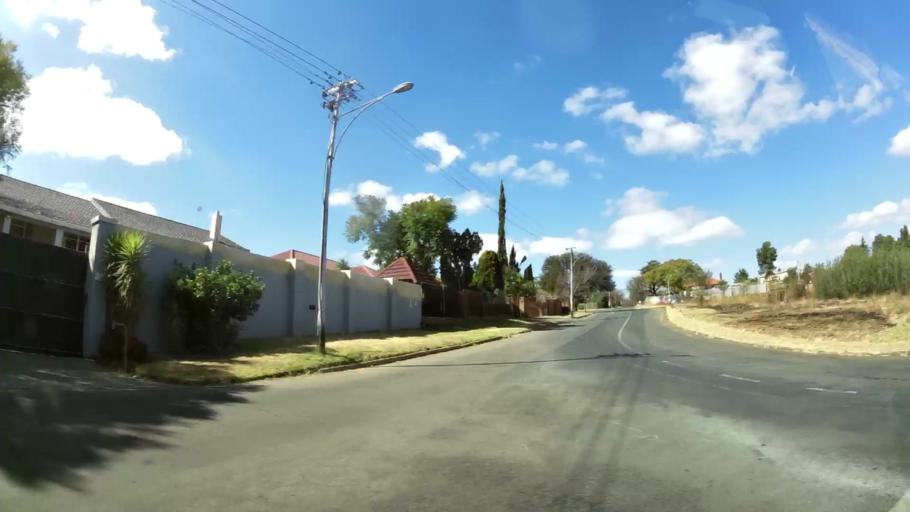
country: ZA
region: Gauteng
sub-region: West Rand District Municipality
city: Krugersdorp
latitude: -26.0961
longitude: 27.7853
